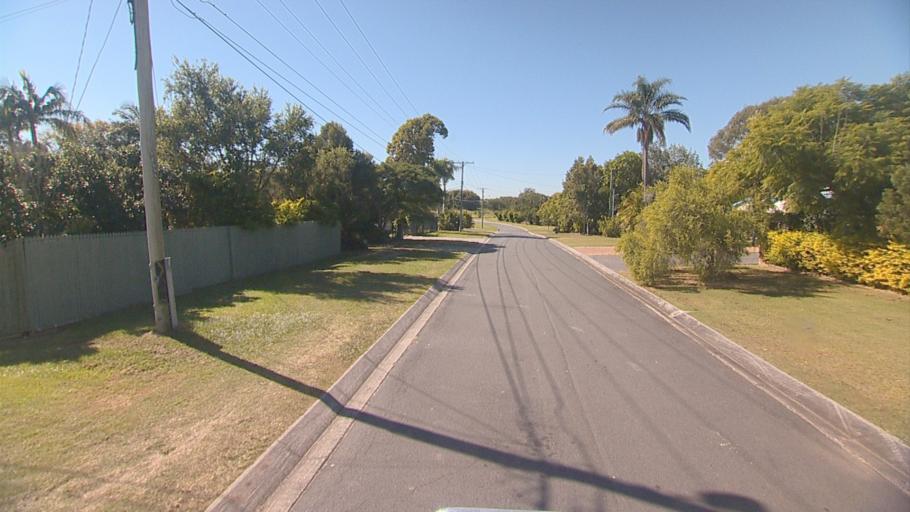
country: AU
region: Queensland
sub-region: Logan
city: Waterford West
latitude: -27.6898
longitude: 153.1406
